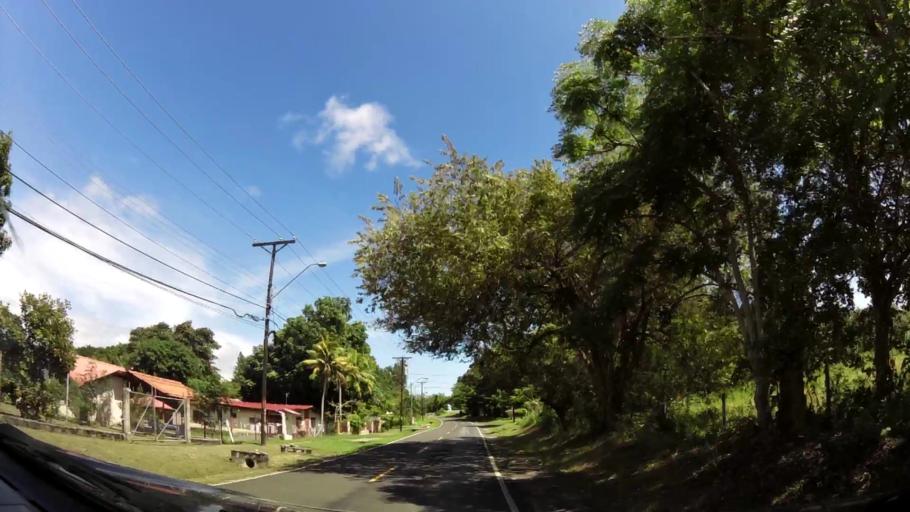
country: PA
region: Panama
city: Nueva Gorgona
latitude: 8.5590
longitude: -79.8857
